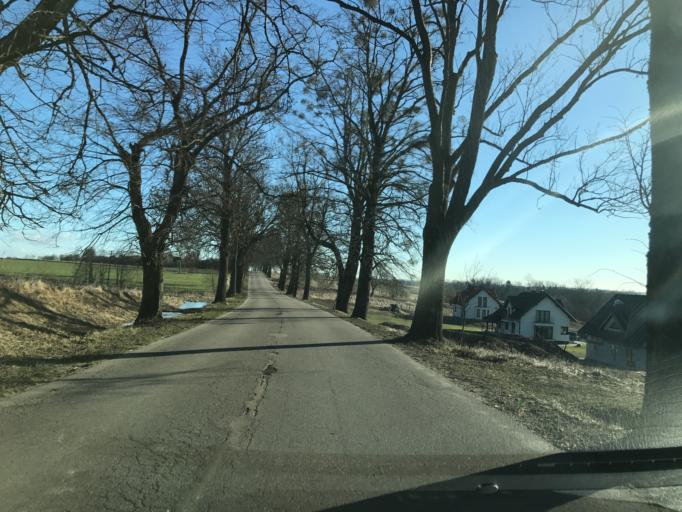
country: PL
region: Warmian-Masurian Voivodeship
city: Dobre Miasto
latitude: 53.9620
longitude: 20.3571
